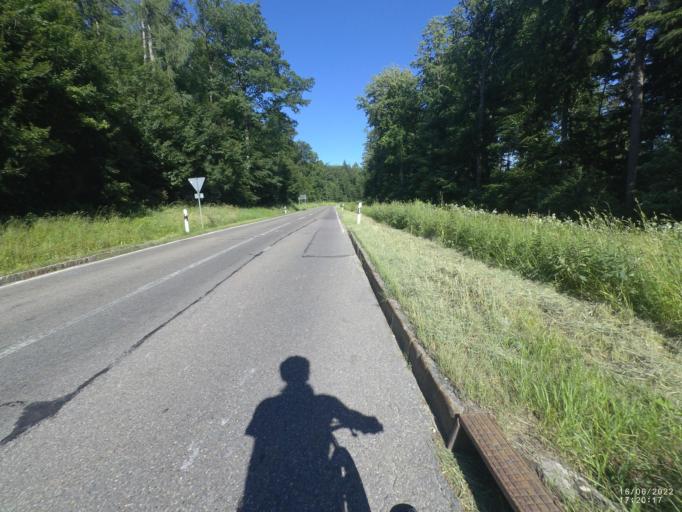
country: DE
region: Baden-Wuerttemberg
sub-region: Regierungsbezirk Stuttgart
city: Gerstetten
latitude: 48.6115
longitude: 10.0270
